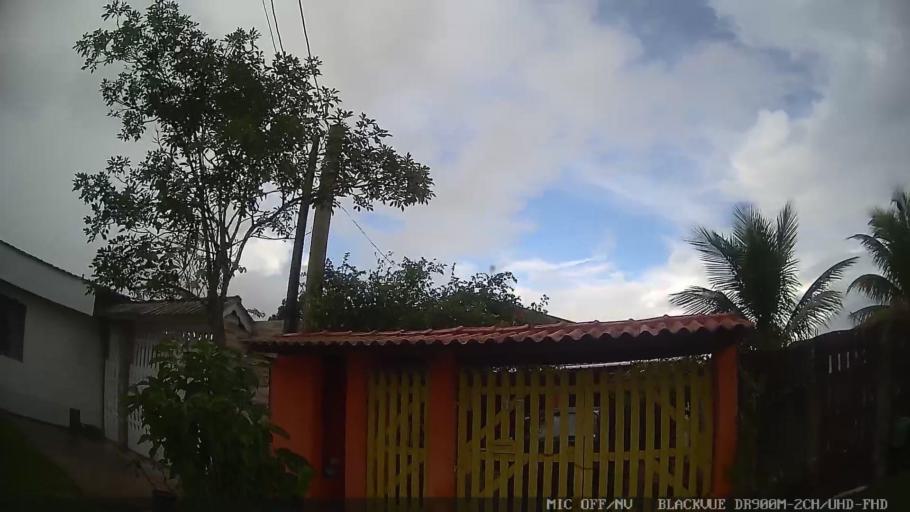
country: BR
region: Sao Paulo
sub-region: Itanhaem
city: Itanhaem
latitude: -24.2112
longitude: -46.8605
